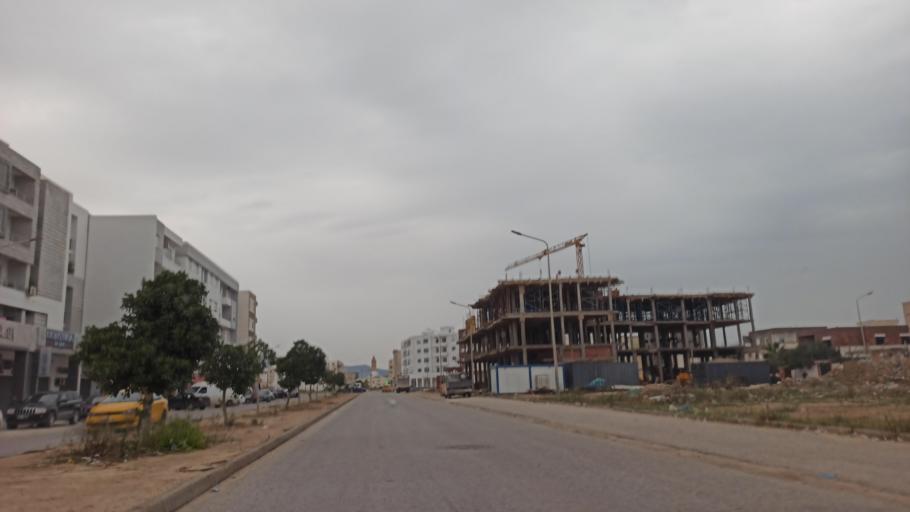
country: TN
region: Tunis
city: Hammam-Lif
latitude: 36.7049
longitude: 10.4158
